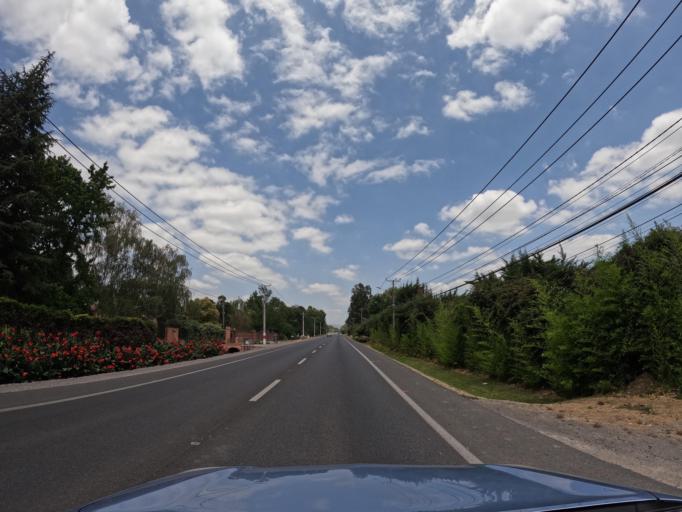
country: CL
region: Maule
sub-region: Provincia de Curico
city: Curico
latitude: -35.0097
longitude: -71.2204
